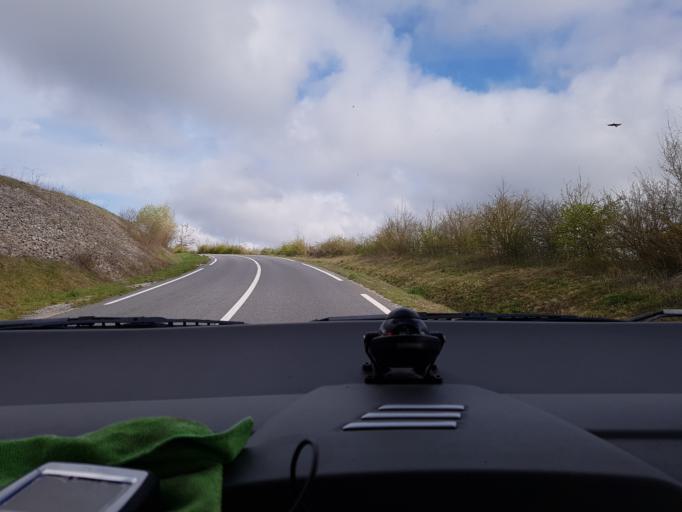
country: FR
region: Midi-Pyrenees
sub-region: Departement de l'Aveyron
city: Moyrazes
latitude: 44.3774
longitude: 2.4583
